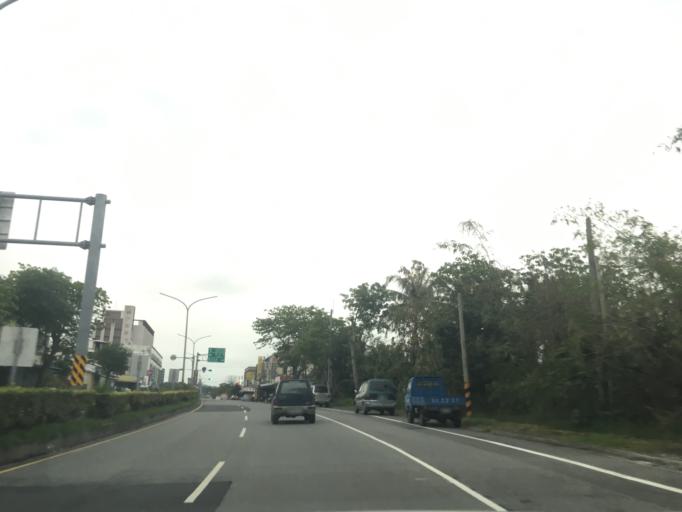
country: TW
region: Taiwan
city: Taitung City
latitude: 22.7052
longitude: 121.0413
